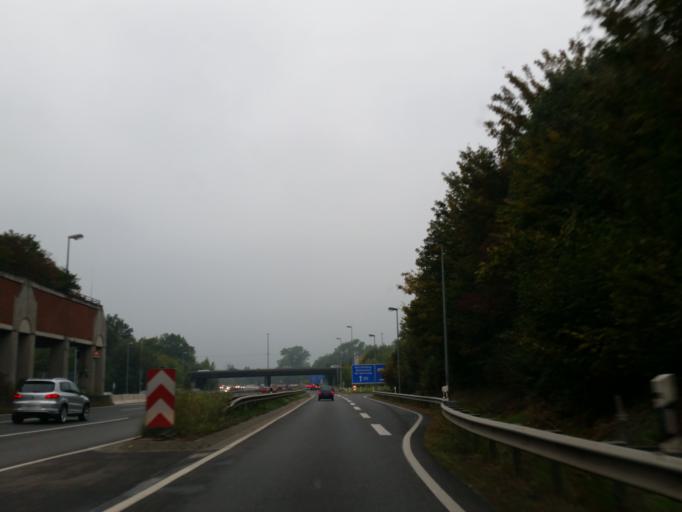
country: DE
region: Lower Saxony
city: Braunschweig
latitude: 52.2368
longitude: 10.5316
